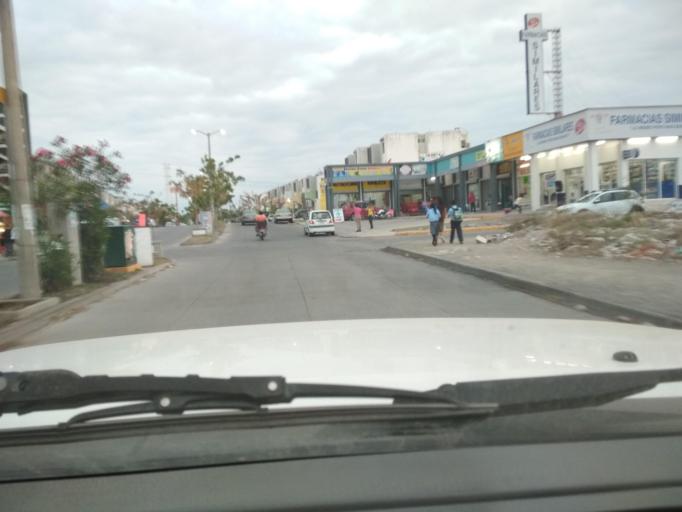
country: MX
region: Veracruz
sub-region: Medellin
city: Fraccionamiento Arboledas San Ramon
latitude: 19.0930
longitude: -96.1644
